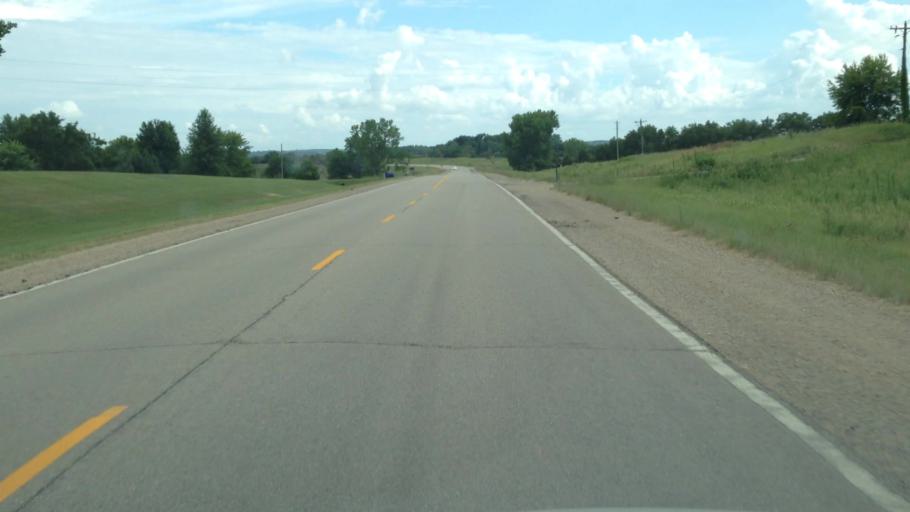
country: US
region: Kansas
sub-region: Shawnee County
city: Topeka
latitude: 39.1058
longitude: -95.4838
